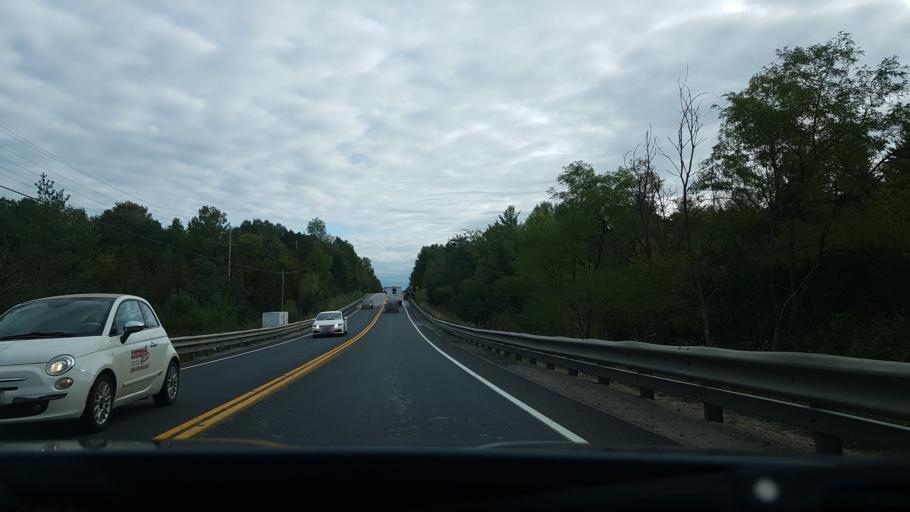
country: CA
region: Ontario
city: Barrie
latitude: 44.5122
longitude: -79.7634
